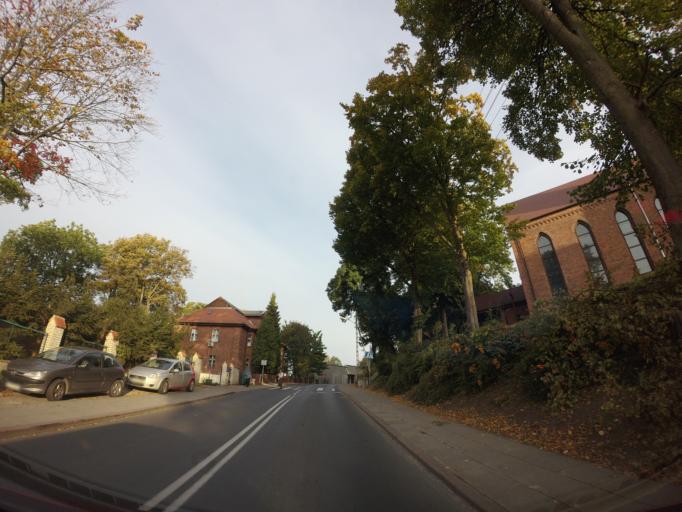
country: PL
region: West Pomeranian Voivodeship
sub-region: Szczecin
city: Szczecin
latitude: 53.4681
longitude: 14.5904
